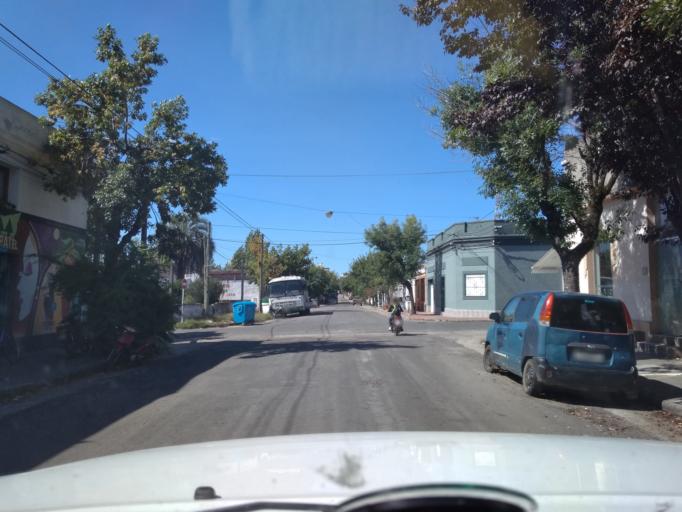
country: UY
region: Florida
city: Florida
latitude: -34.1019
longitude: -56.2195
